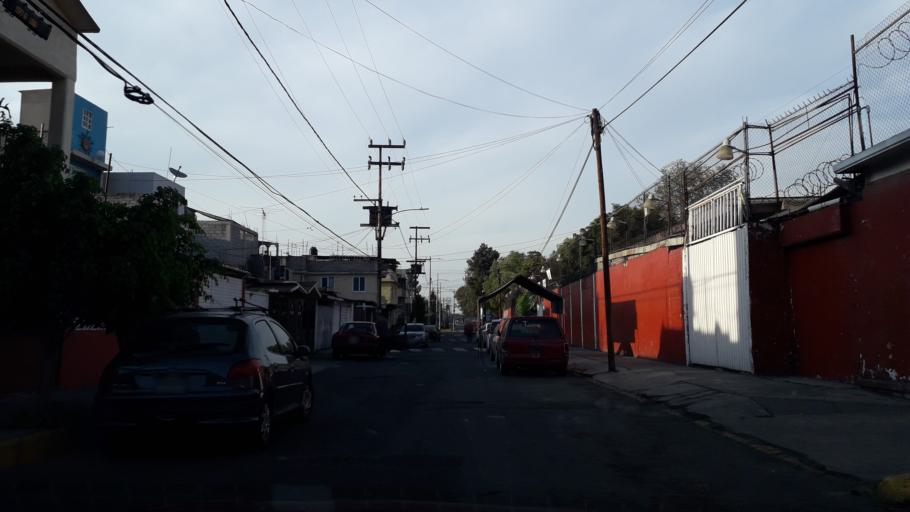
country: MX
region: Mexico City
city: Iztapalapa
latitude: 19.3593
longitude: -99.0544
